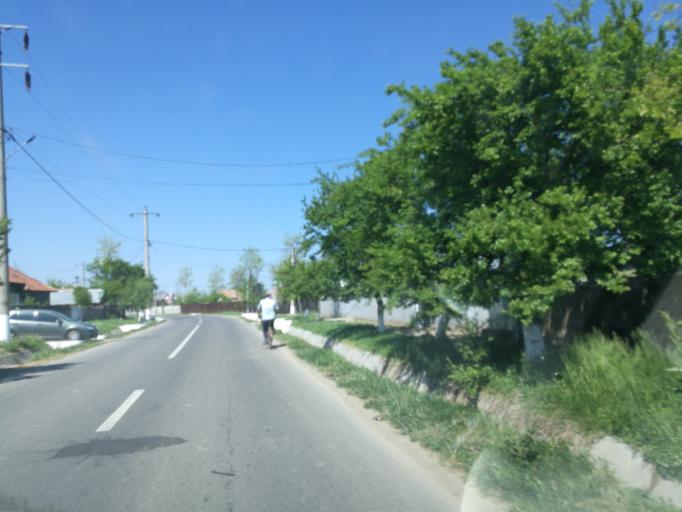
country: RO
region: Ialomita
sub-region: Comuna Adancata
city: Adancata
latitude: 44.7643
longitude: 26.4411
